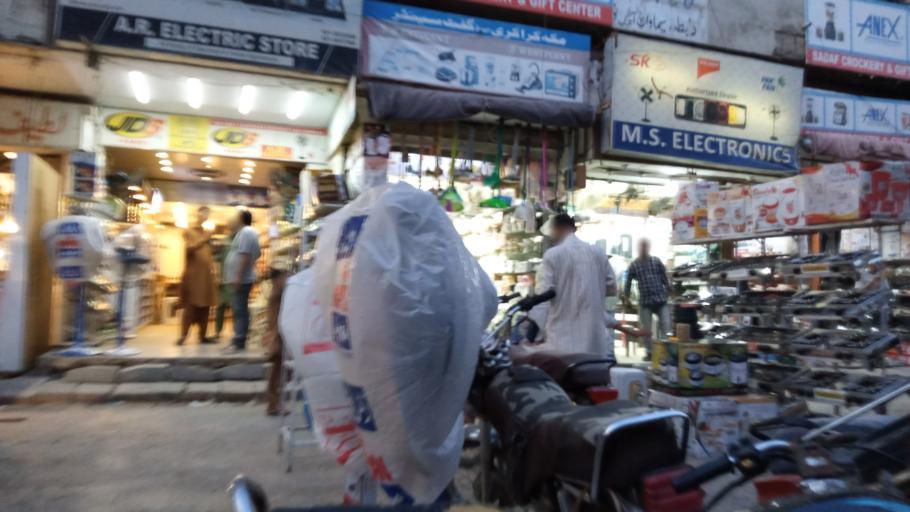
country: PK
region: Sindh
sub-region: Karachi District
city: Karachi
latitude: 24.9368
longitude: 67.0776
